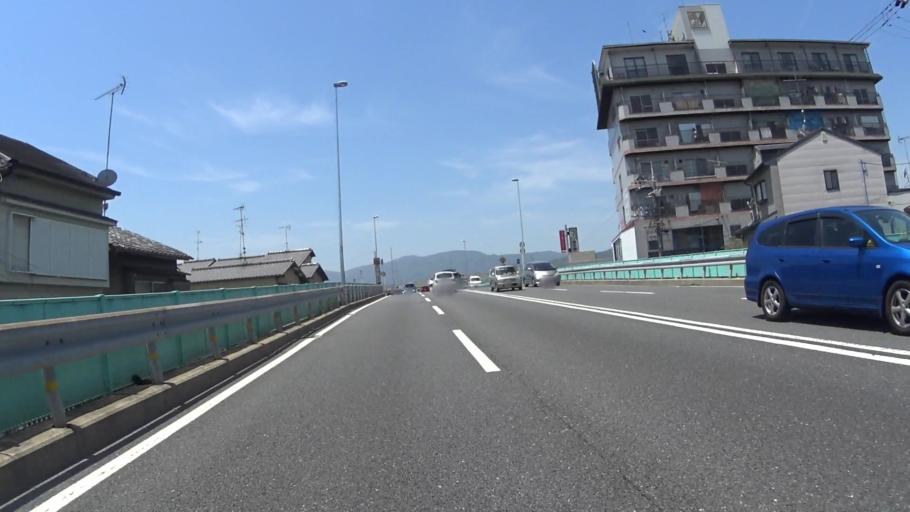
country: JP
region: Kyoto
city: Kameoka
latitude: 35.0239
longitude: 135.5583
